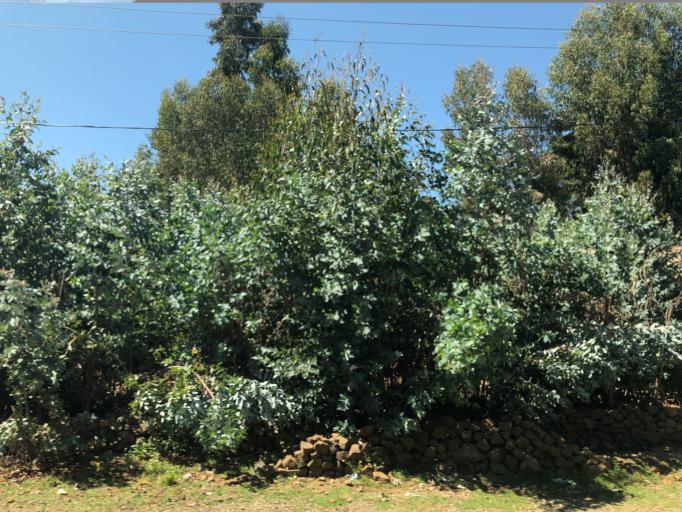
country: ET
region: Amhara
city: Lalibela
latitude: 11.7362
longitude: 38.7550
